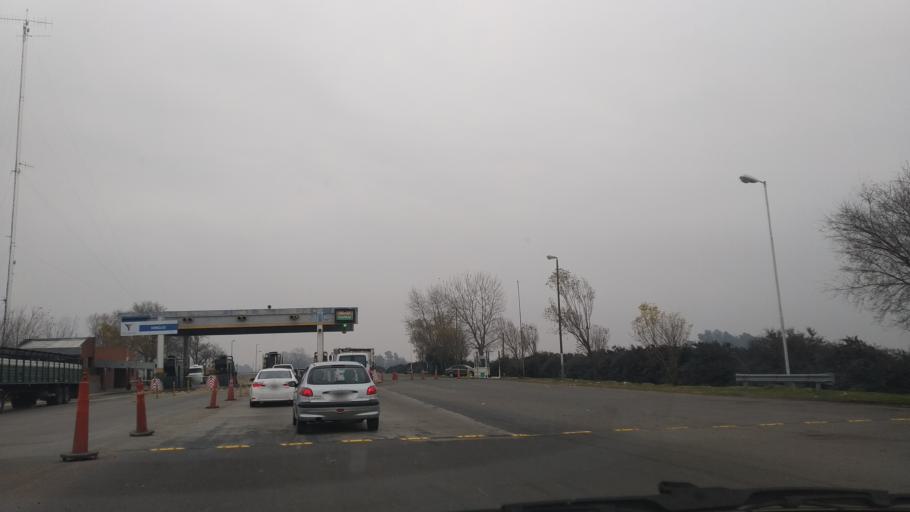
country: AR
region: Buenos Aires
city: Olavarria
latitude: -36.8613
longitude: -60.1222
